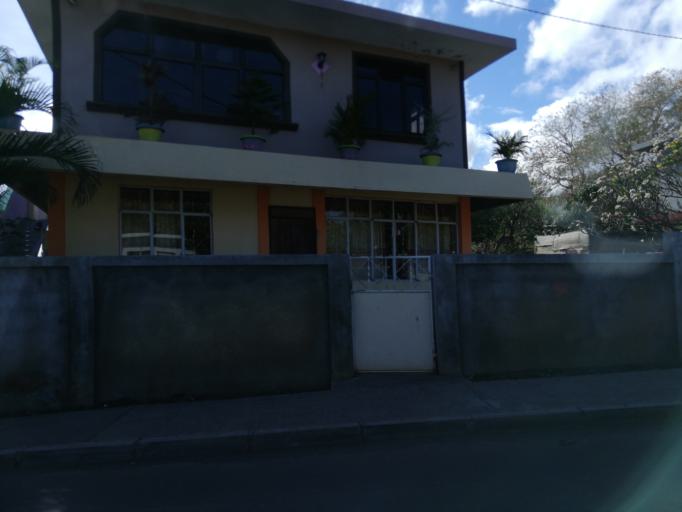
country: MU
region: Moka
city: Pailles
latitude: -20.1777
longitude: 57.4739
